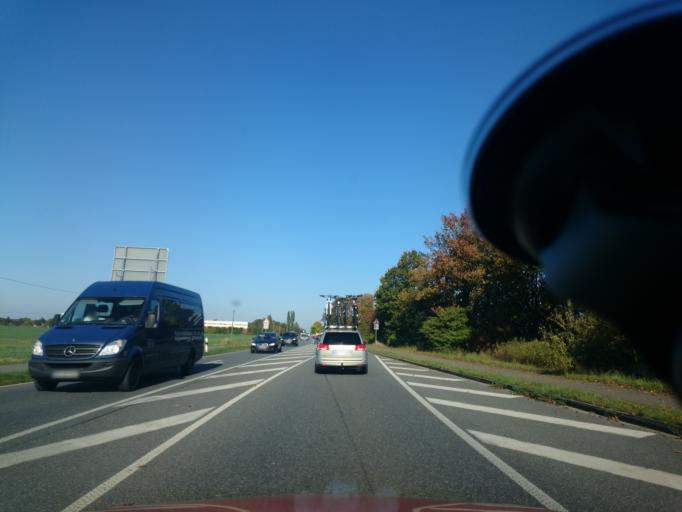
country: DE
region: Mecklenburg-Vorpommern
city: Monchhagen
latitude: 54.1422
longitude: 12.2240
